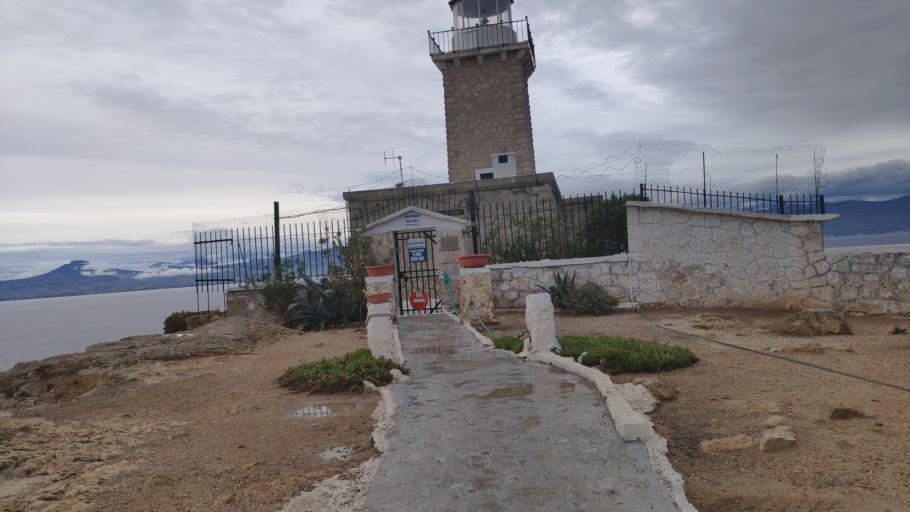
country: GR
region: Peloponnese
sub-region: Nomos Korinthias
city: Vrakhati
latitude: 38.0286
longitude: 22.8503
